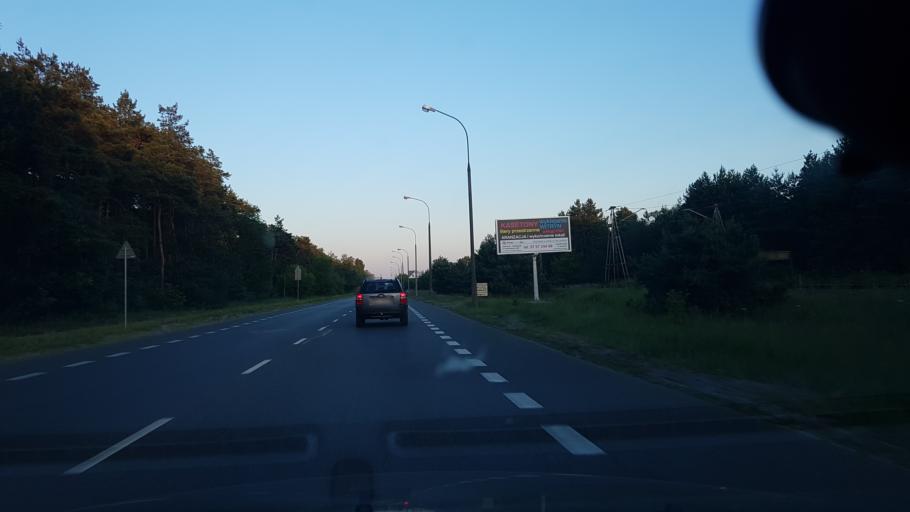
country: PL
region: Masovian Voivodeship
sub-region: Warszawa
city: Wawer
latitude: 52.1976
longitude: 21.1759
